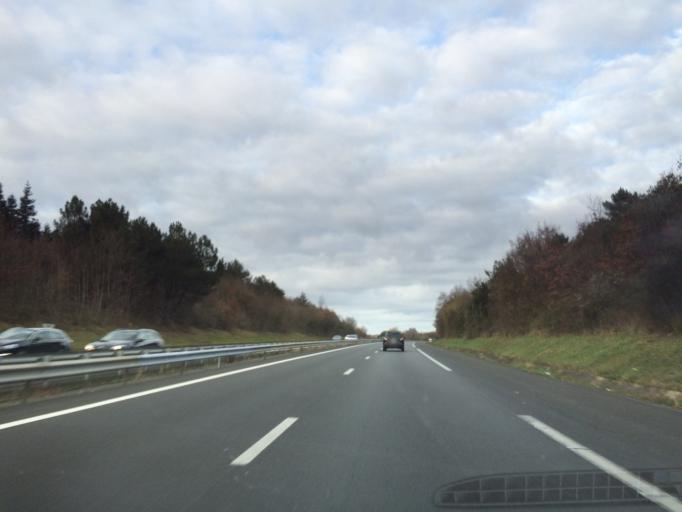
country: FR
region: Poitou-Charentes
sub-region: Departement de la Charente-Maritime
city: Saint-Jean-d'Angely
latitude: 46.0174
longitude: -0.5414
